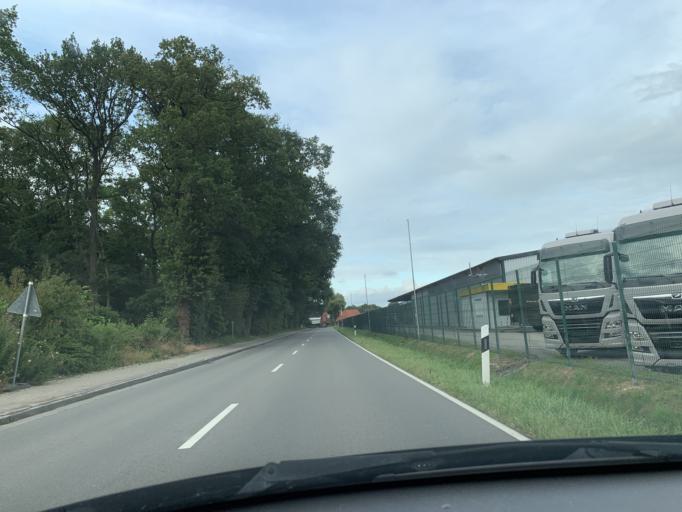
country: DE
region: Lower Saxony
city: Westerstede
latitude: 53.2674
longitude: 7.9372
